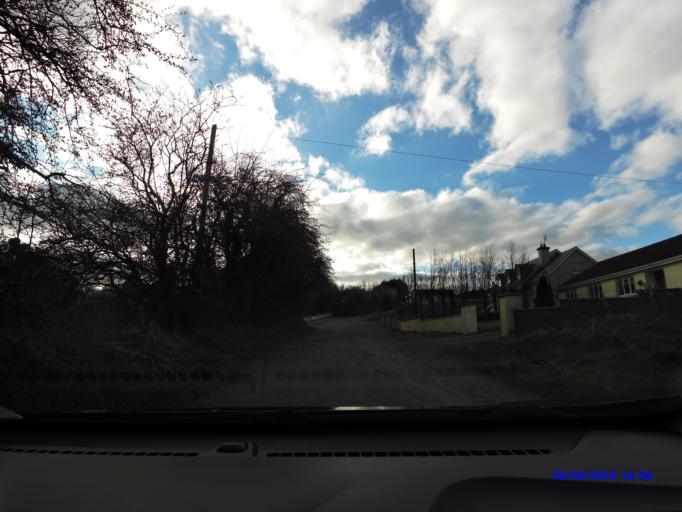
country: IE
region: Connaught
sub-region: Maigh Eo
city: Ballyhaunis
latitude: 53.7585
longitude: -8.7771
